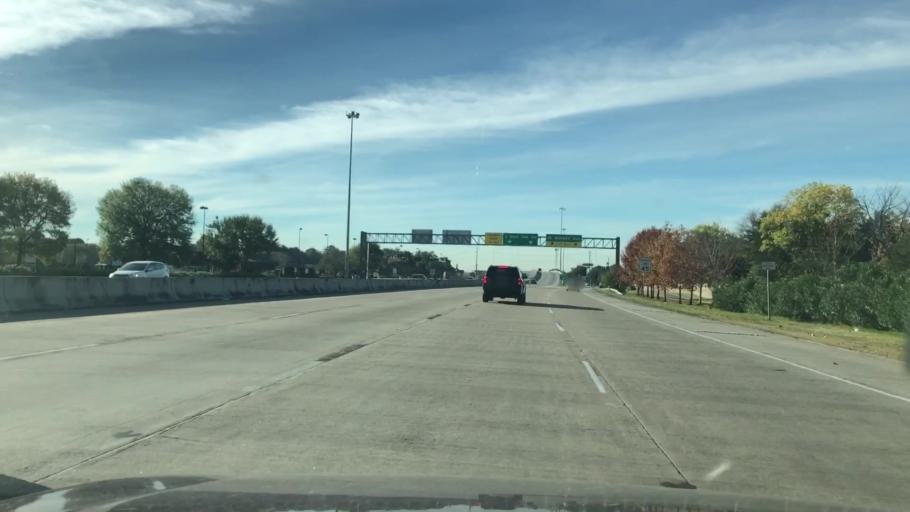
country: US
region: Texas
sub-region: Harris County
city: Bellaire
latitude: 29.6746
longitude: -95.4603
